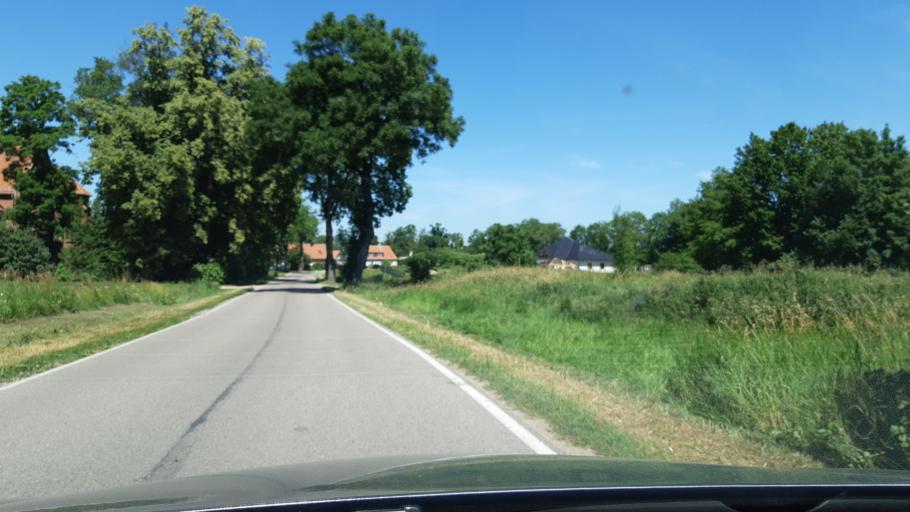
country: PL
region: Warmian-Masurian Voivodeship
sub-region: Powiat gizycki
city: Ryn
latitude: 53.8929
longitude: 21.6611
